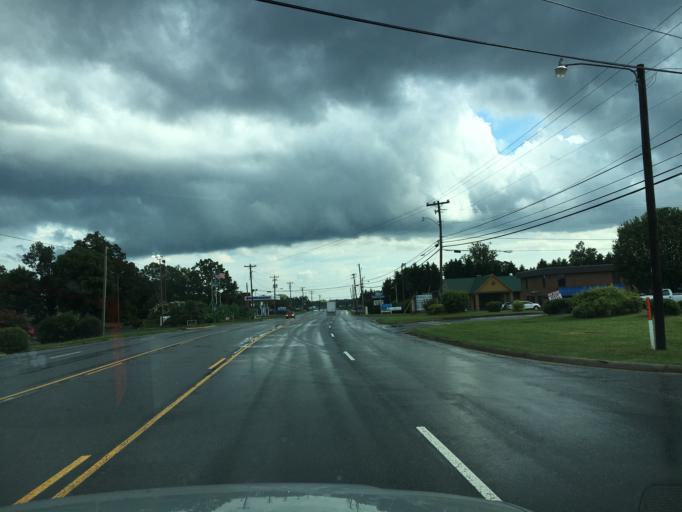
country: US
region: North Carolina
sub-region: Catawba County
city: Conover
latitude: 35.7012
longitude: -81.2619
